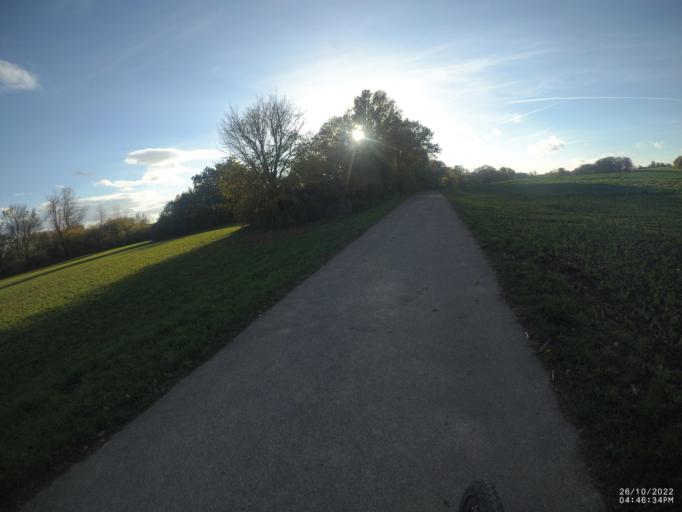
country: DE
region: Baden-Wuerttemberg
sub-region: Regierungsbezirk Stuttgart
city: Hohenstadt
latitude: 48.5381
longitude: 9.6759
